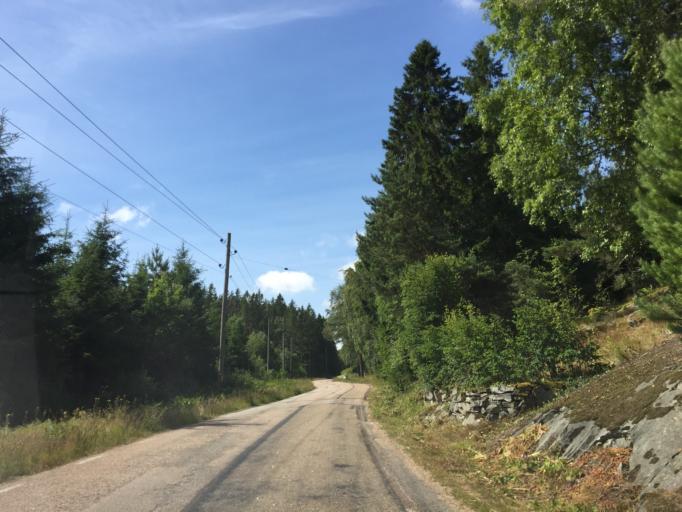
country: SE
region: Vaestra Goetaland
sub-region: Orust
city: Henan
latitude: 58.2970
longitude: 11.6594
